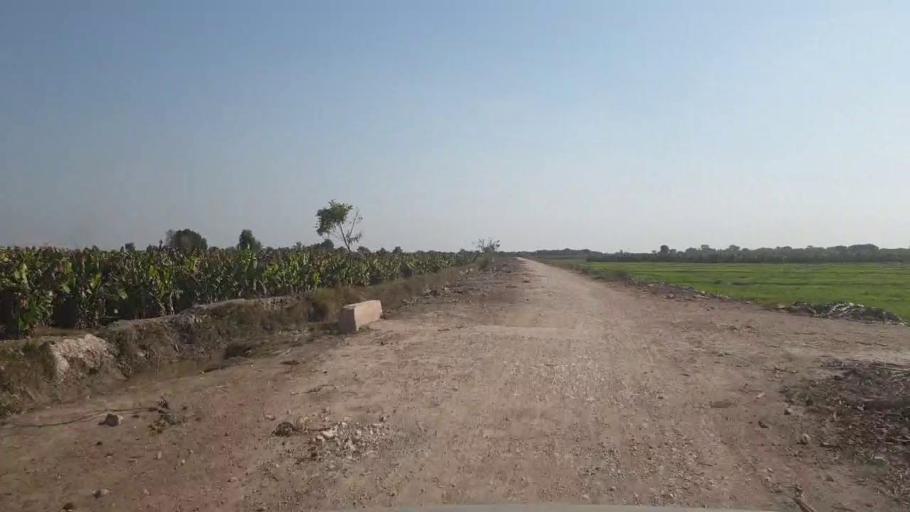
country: PK
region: Sindh
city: Chambar
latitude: 25.3160
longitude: 68.8723
